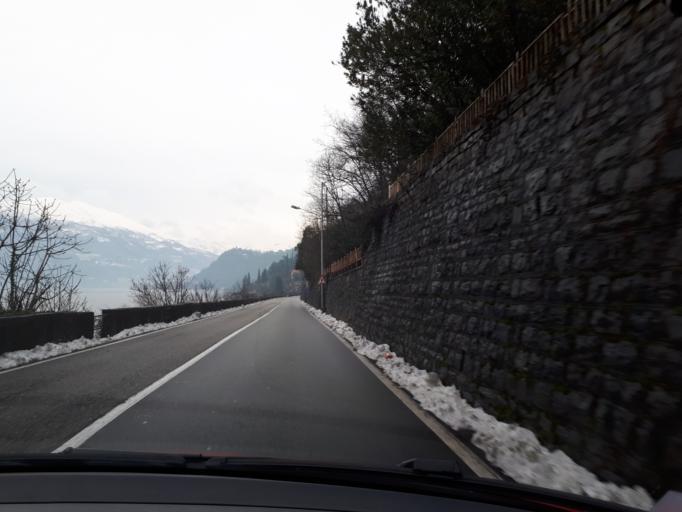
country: IT
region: Lombardy
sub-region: Provincia di Lecco
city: Varenna
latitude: 45.9875
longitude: 9.2922
